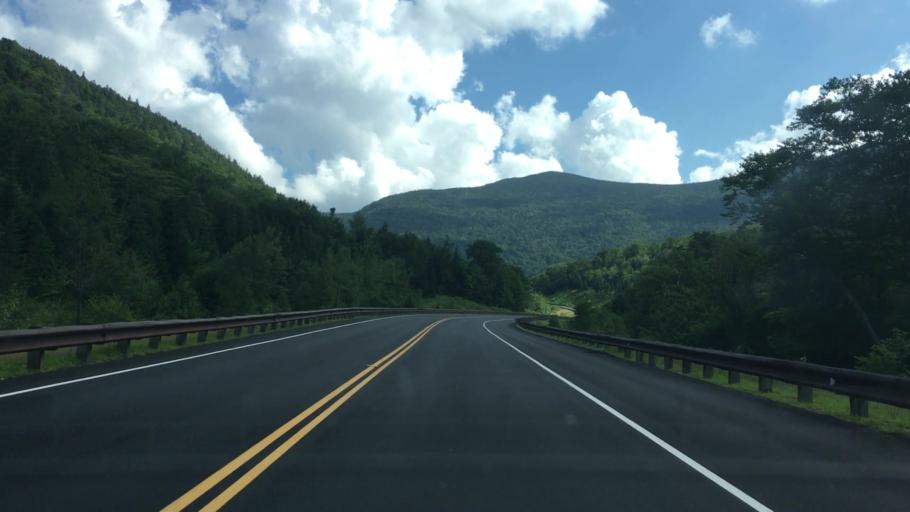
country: US
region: New Hampshire
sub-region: Grafton County
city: Woodstock
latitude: 44.0504
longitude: -71.7929
